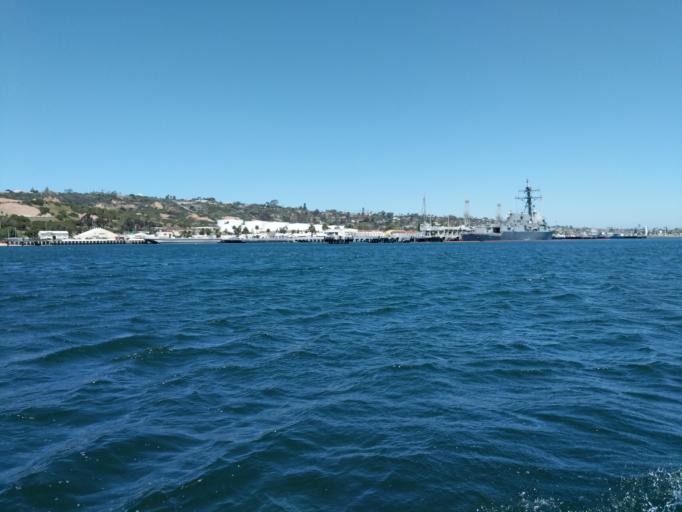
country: US
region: California
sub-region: San Diego County
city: Coronado
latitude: 32.6969
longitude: -117.2352
